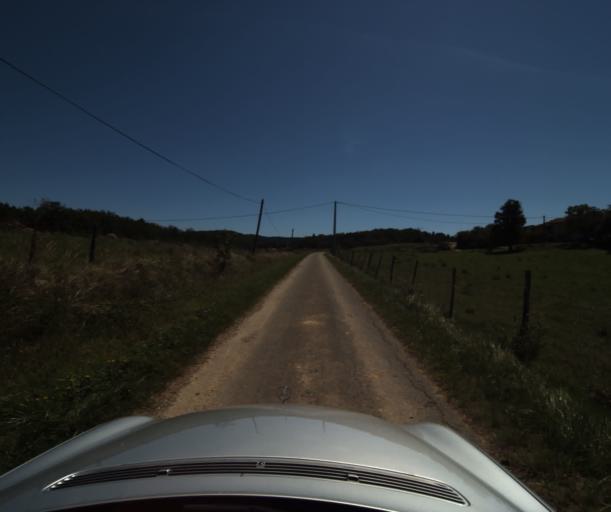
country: FR
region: Languedoc-Roussillon
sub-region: Departement de l'Aude
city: Chalabre
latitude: 42.9947
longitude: 1.9334
